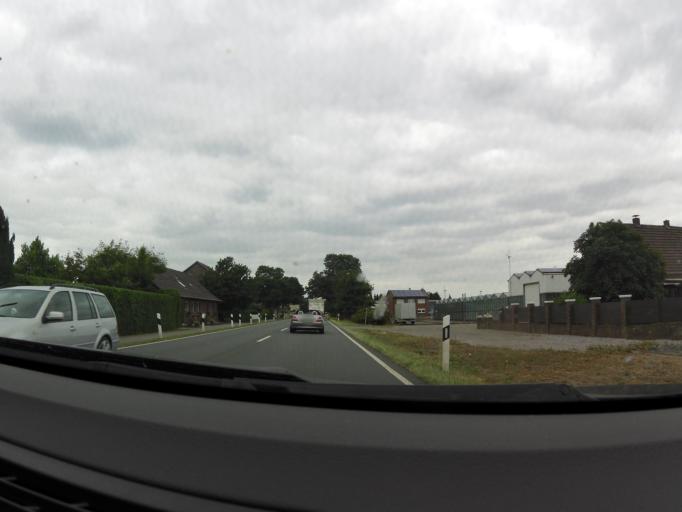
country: DE
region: North Rhine-Westphalia
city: Straelen
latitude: 51.4603
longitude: 6.2777
